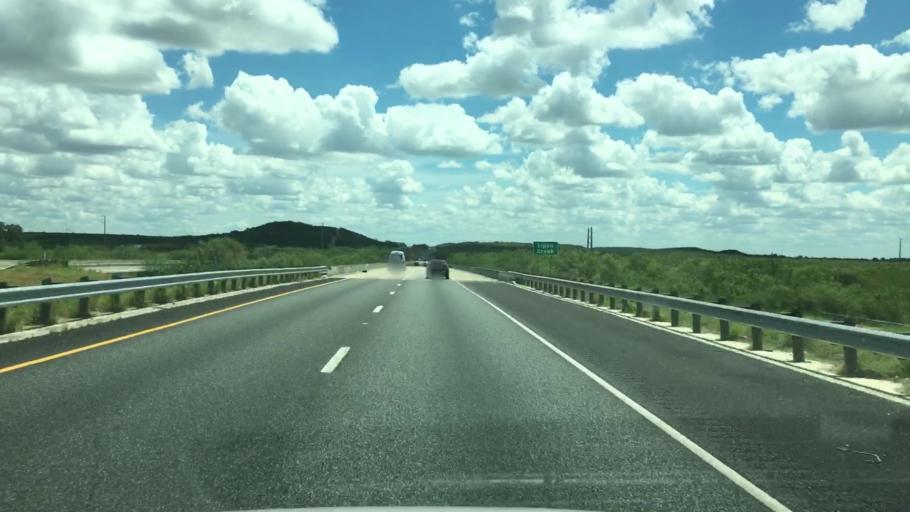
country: US
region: Texas
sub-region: Live Oak County
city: Three Rivers
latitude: 28.7326
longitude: -98.2890
